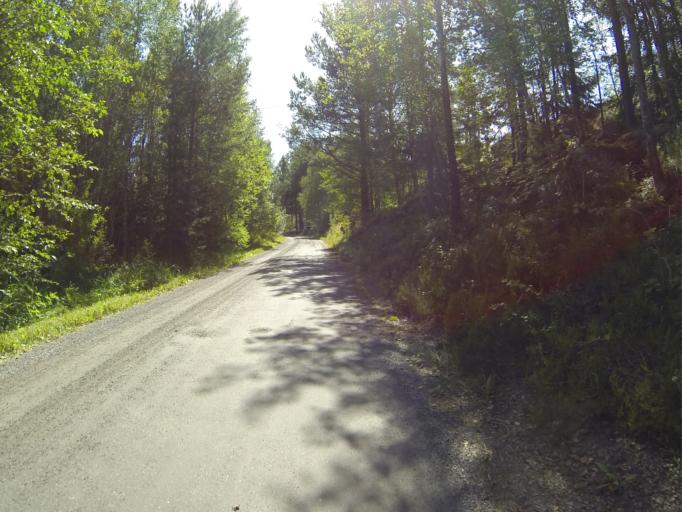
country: FI
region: Varsinais-Suomi
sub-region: Salo
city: Saerkisalo
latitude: 60.2628
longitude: 22.9734
